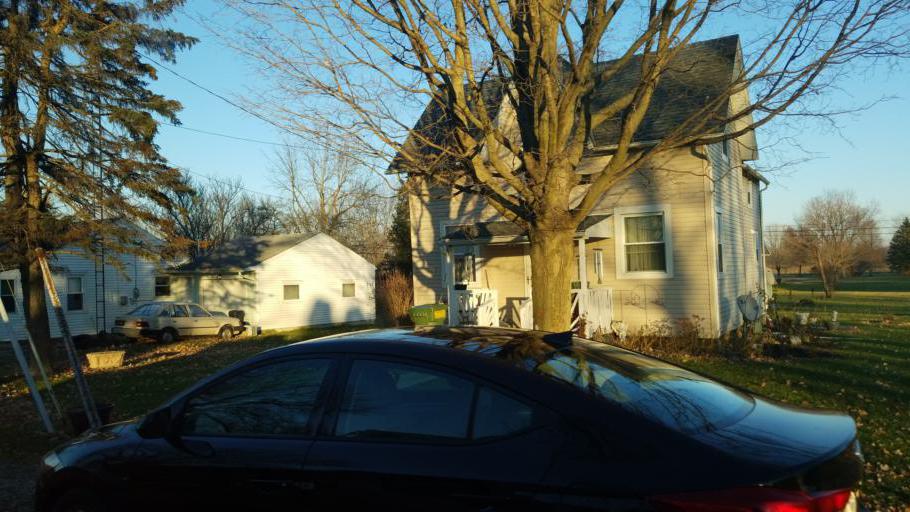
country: US
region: Ohio
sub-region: Wyandot County
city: Upper Sandusky
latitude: 40.8124
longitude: -83.1329
